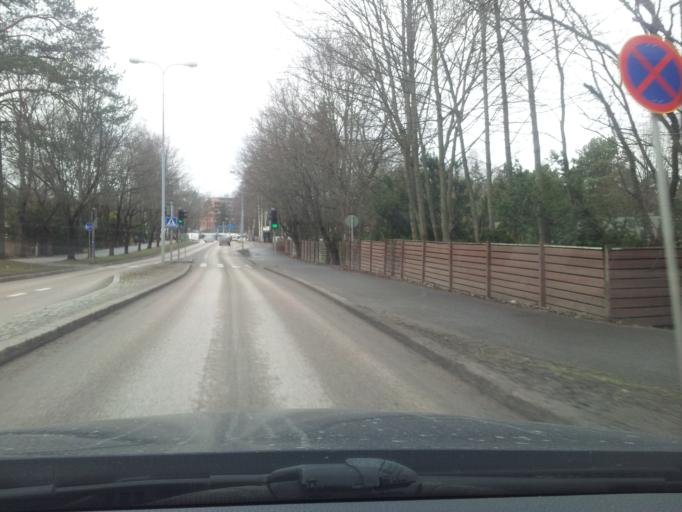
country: FI
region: Uusimaa
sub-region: Helsinki
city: Otaniemi
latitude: 60.1804
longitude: 24.7972
